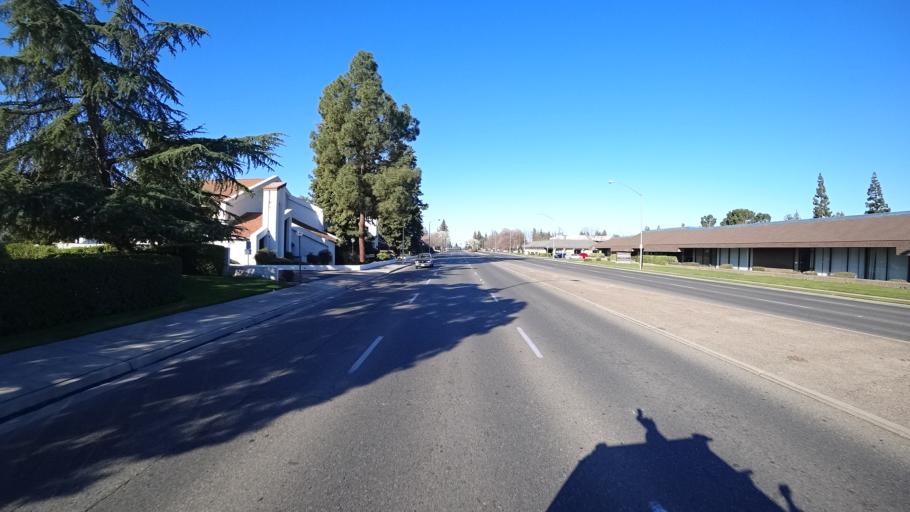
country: US
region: California
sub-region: Fresno County
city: Fresno
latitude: 36.8081
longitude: -119.8343
